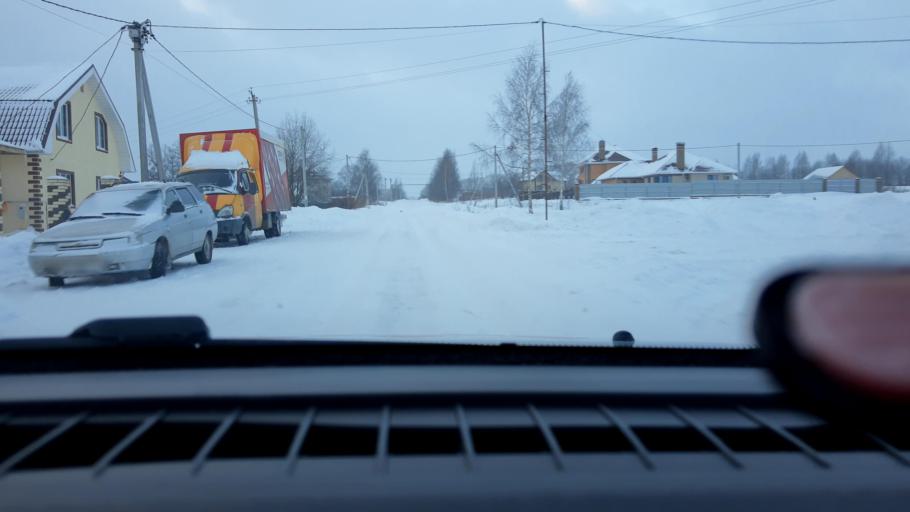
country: RU
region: Nizjnij Novgorod
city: Burevestnik
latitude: 56.1503
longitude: 43.7602
